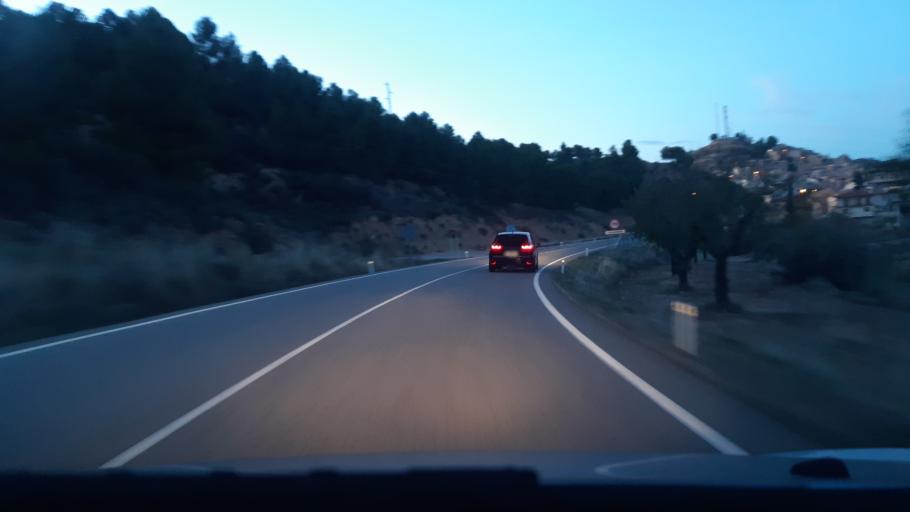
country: ES
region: Aragon
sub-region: Provincia de Teruel
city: Calaceite
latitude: 41.0109
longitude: 0.1872
